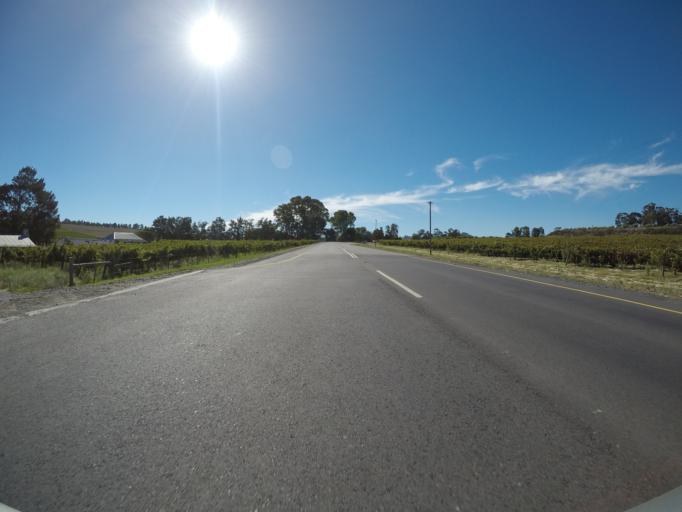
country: ZA
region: Western Cape
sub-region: Cape Winelands District Municipality
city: Stellenbosch
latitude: -33.9886
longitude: 18.7574
